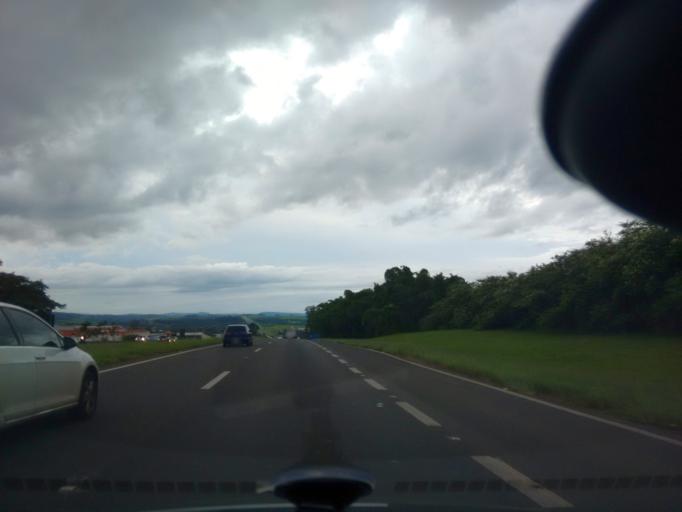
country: BR
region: Sao Paulo
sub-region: Rio Claro
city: Rio Claro
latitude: -22.4048
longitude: -47.5891
